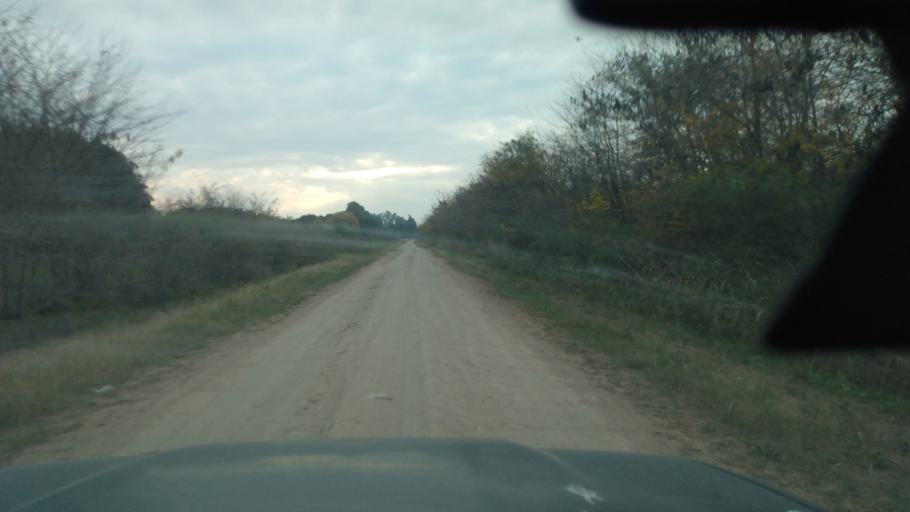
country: AR
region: Buenos Aires
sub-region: Partido de Lujan
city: Lujan
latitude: -34.5644
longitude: -59.1528
